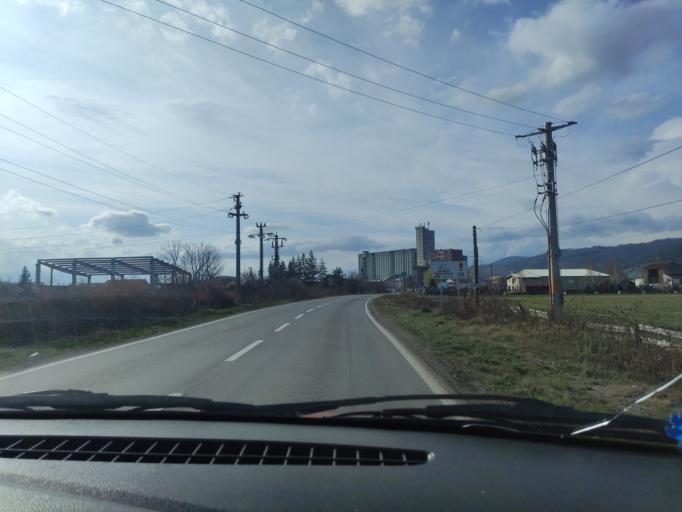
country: RO
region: Brasov
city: Codlea
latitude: 45.7109
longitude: 25.4631
